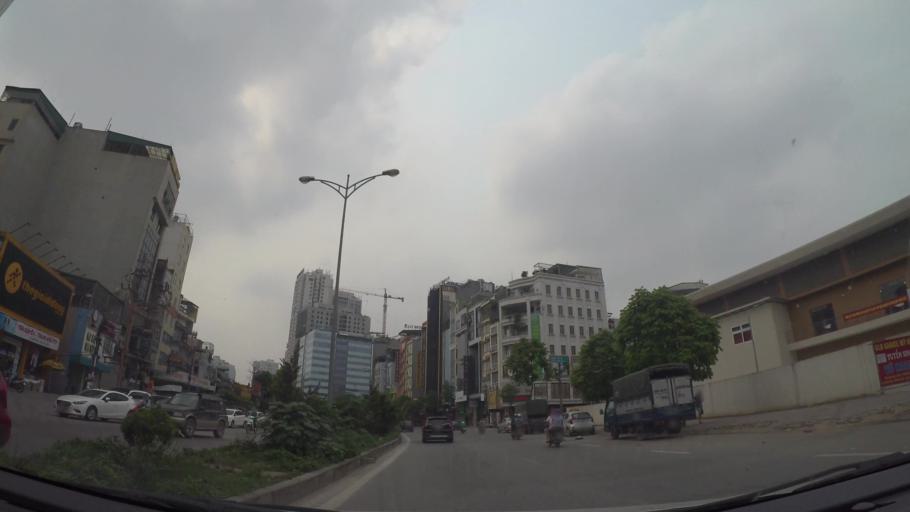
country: VN
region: Ha Noi
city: Cau Dien
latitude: 21.0323
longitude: 105.7737
